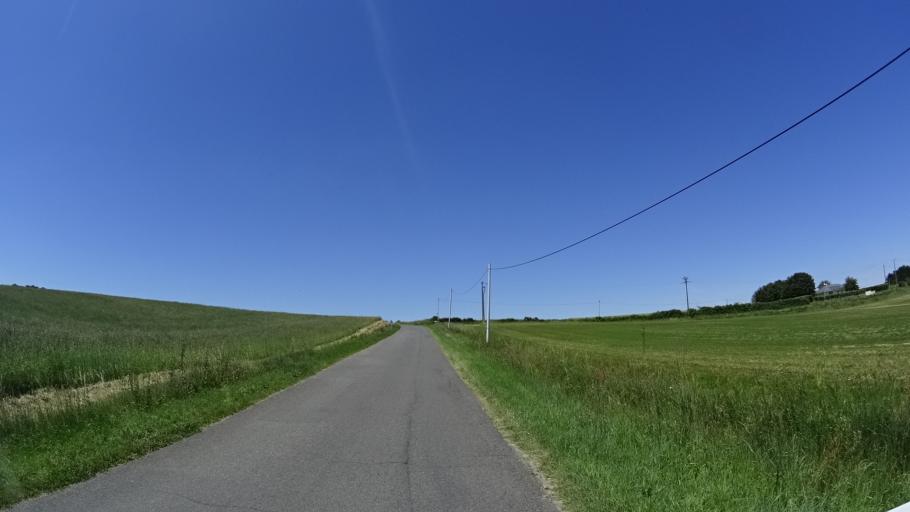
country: FR
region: Pays de la Loire
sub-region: Departement de Maine-et-Loire
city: Chenehutte-Treves-Cunault
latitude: 47.2836
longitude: -0.1383
